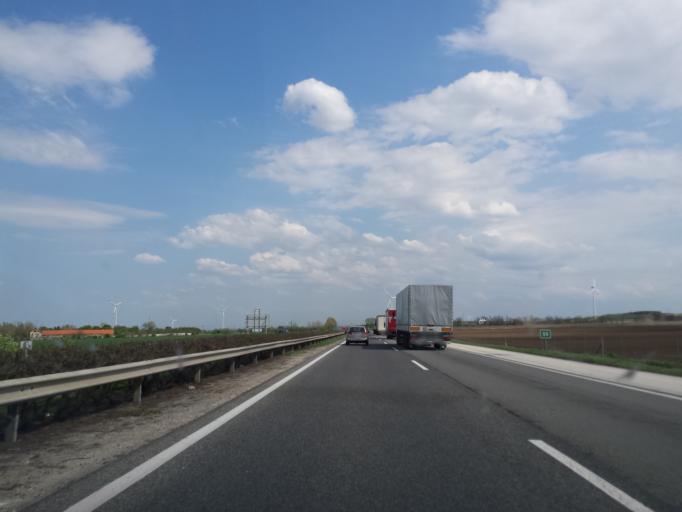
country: HU
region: Gyor-Moson-Sopron
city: Bony
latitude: 47.6813
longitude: 17.9061
